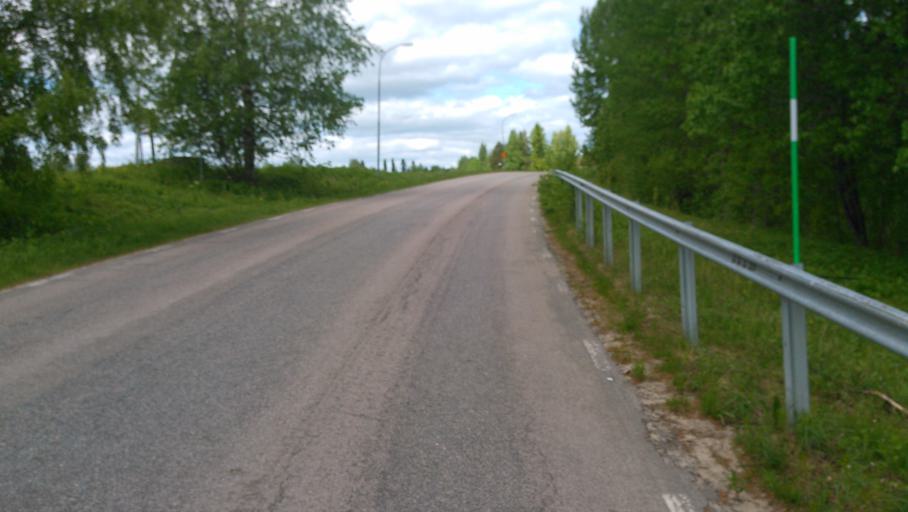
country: SE
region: Vaesterbotten
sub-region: Umea Kommun
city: Roback
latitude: 63.8700
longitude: 20.0666
